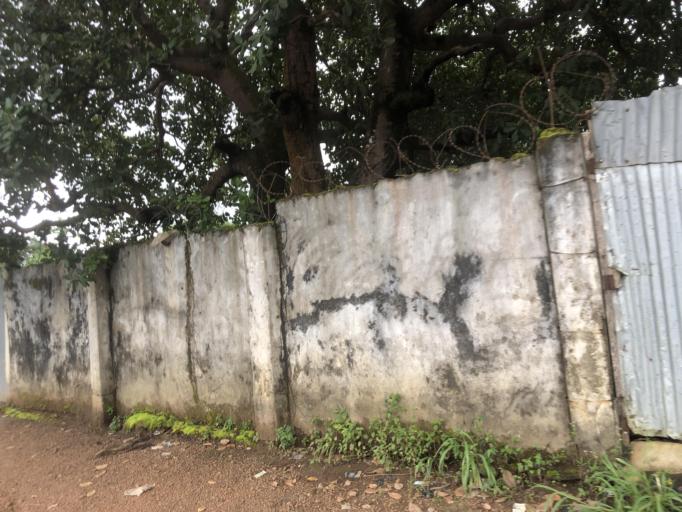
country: SL
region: Northern Province
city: Makeni
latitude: 8.9111
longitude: -12.0438
